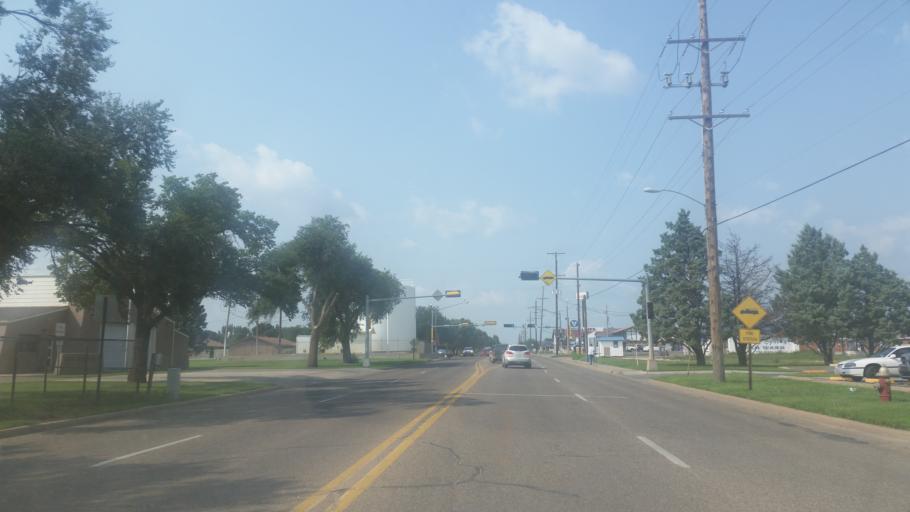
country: US
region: New Mexico
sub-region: Curry County
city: Clovis
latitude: 34.4108
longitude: -103.1789
